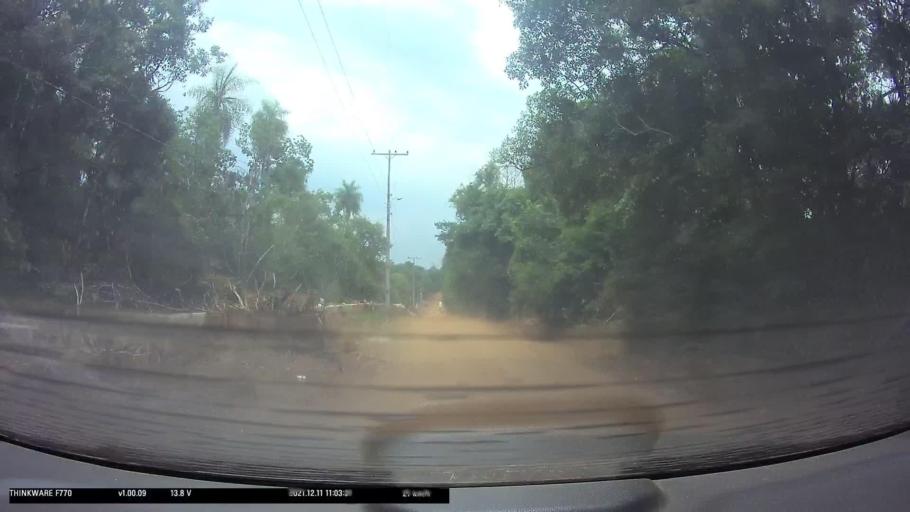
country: PY
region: Cordillera
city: Altos
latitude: -25.3035
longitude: -57.2442
